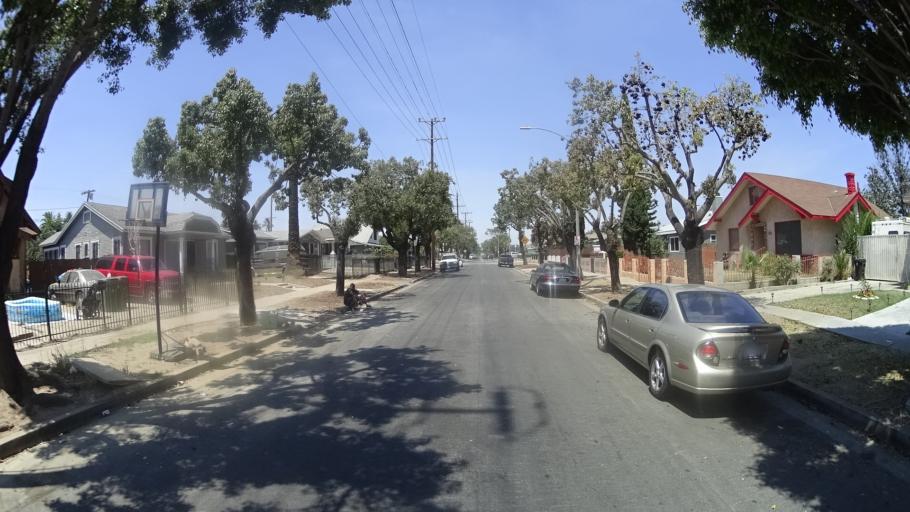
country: US
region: California
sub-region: Los Angeles County
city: Westmont
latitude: 33.9694
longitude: -118.2930
